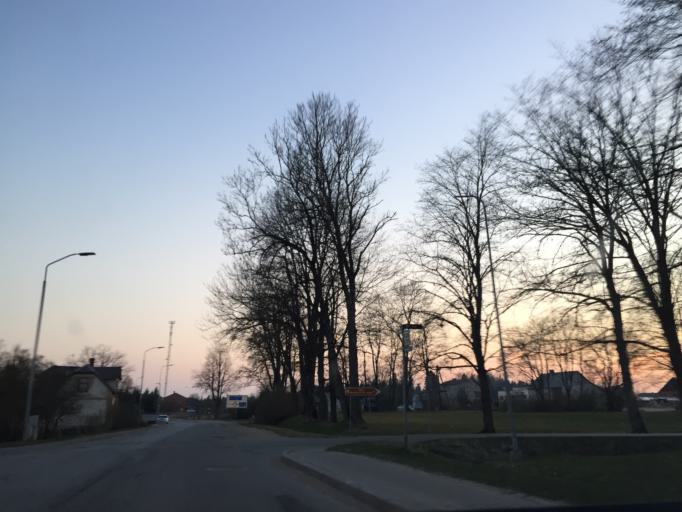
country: LV
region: Valkas Rajons
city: Valka
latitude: 57.7675
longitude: 26.0081
